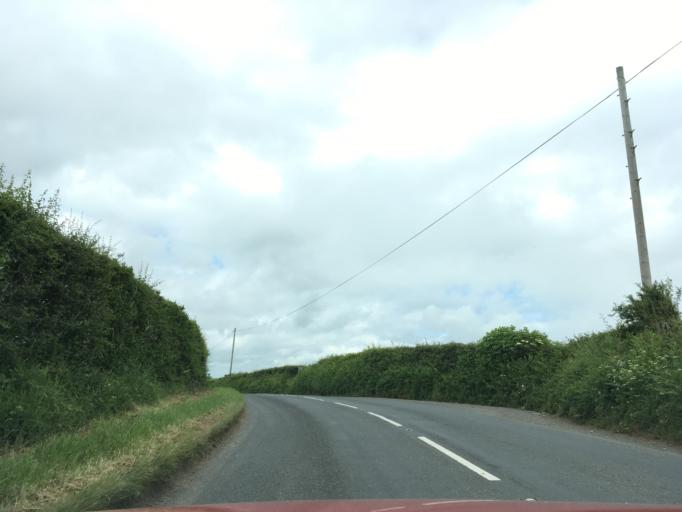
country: GB
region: England
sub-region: Devon
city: Dartmouth
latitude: 50.3370
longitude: -3.5908
